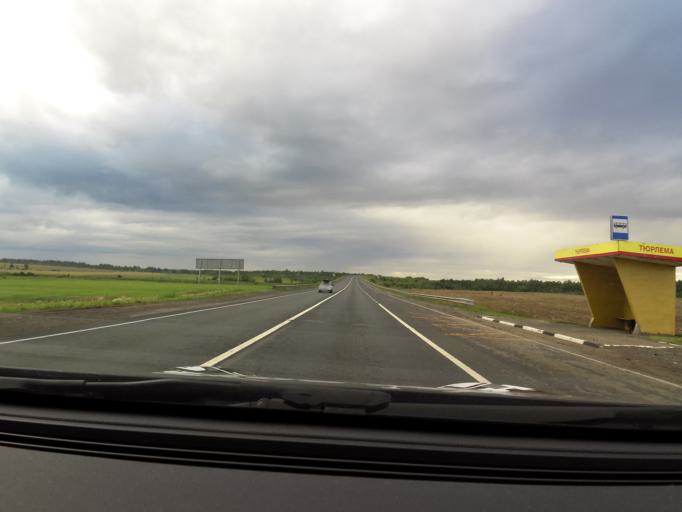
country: RU
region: Chuvashia
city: Kozlovka
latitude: 55.7493
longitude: 48.2197
